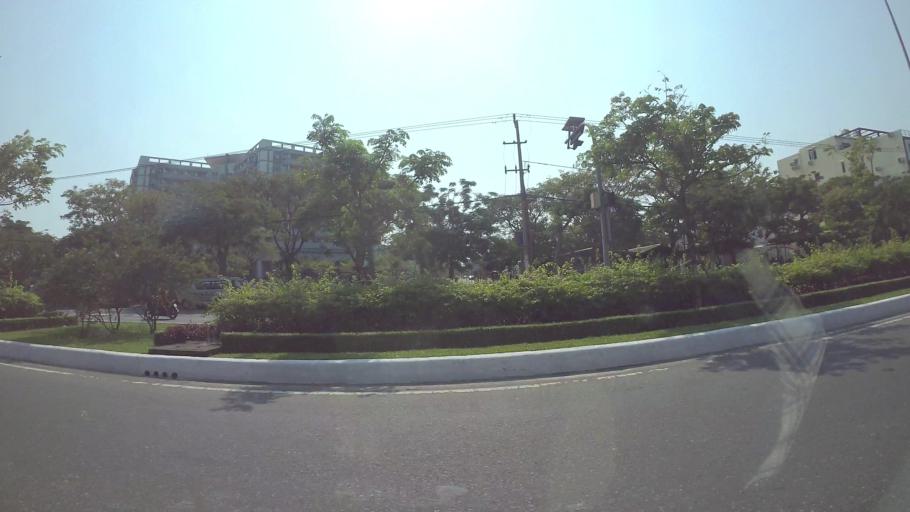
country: VN
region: Da Nang
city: Ngu Hanh Son
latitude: 16.0241
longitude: 108.2502
